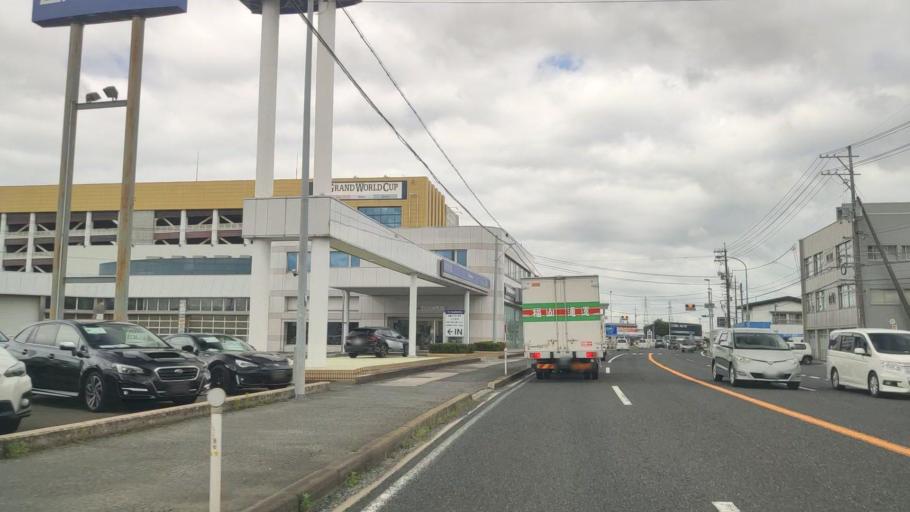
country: JP
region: Tottori
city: Yonago
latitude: 35.4289
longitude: 133.3755
